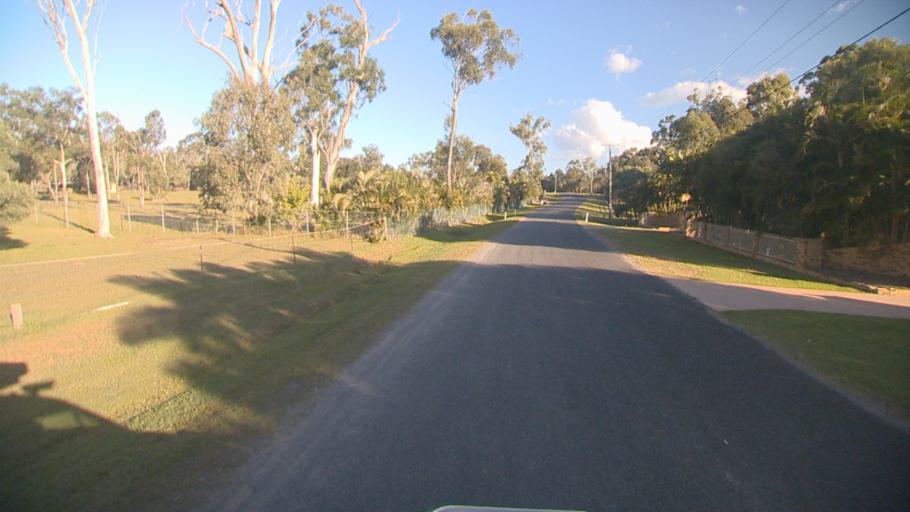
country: AU
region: Queensland
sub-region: Redland
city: Redland Bay
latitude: -27.6597
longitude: 153.2675
